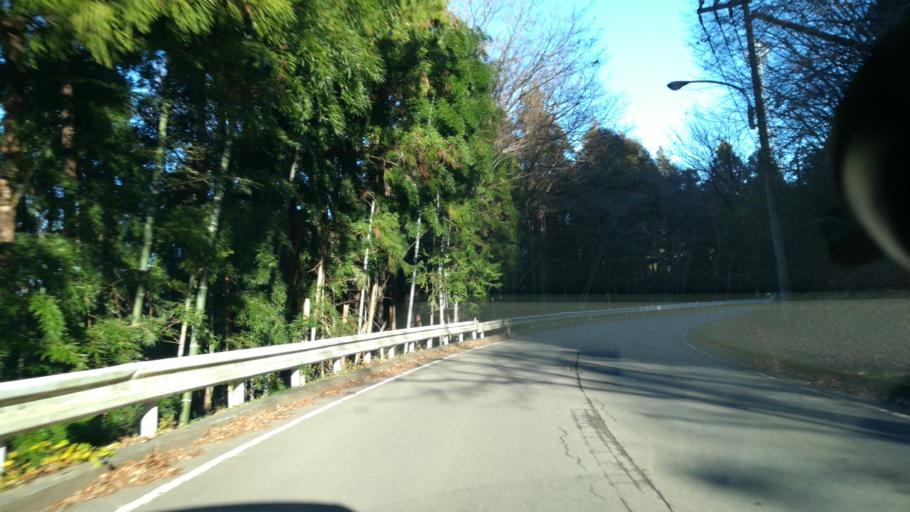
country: JP
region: Tokyo
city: Hachioji
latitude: 35.5536
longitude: 139.2590
